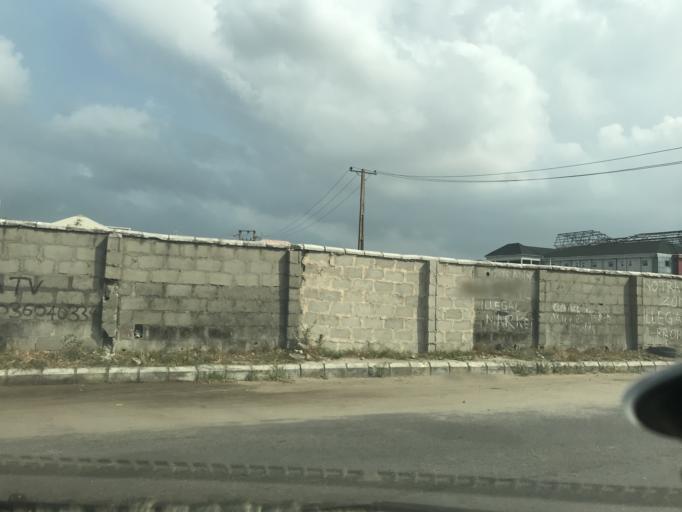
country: NG
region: Lagos
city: Ikoyi
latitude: 6.4240
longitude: 3.4450
